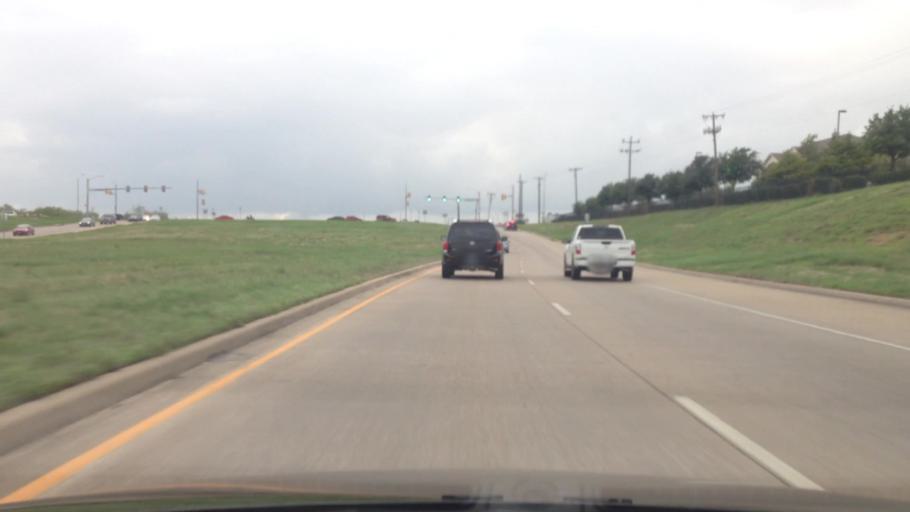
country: US
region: Texas
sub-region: Tarrant County
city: Crowley
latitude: 32.5779
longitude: -97.3263
